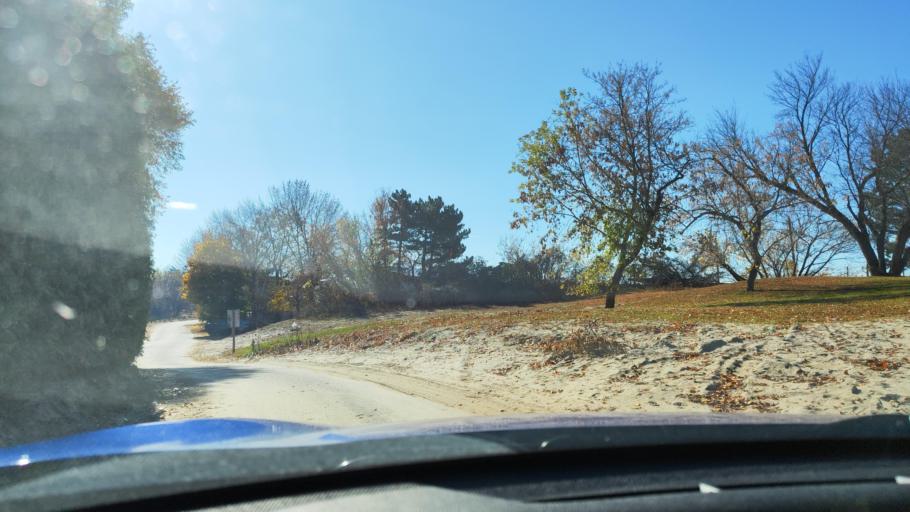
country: CA
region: Ontario
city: Wasaga Beach
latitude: 44.5256
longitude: -80.0169
